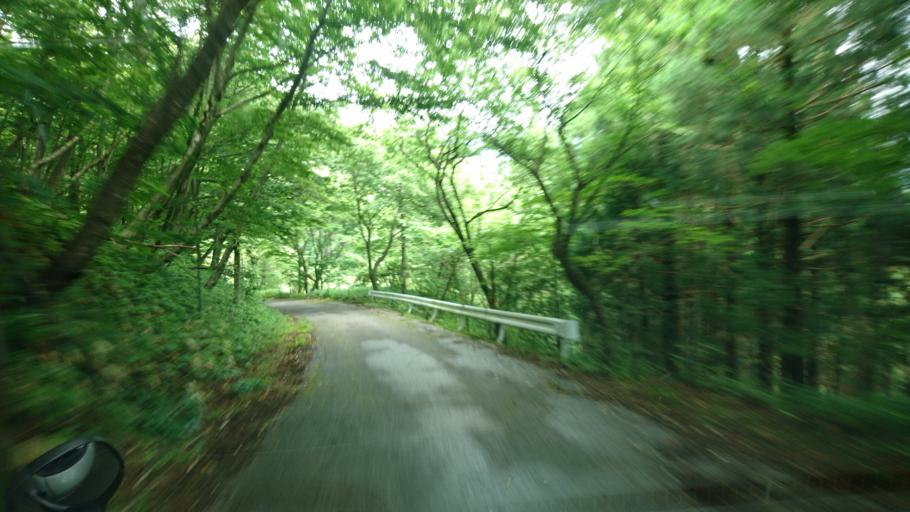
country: JP
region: Iwate
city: Ofunato
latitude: 39.1337
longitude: 141.7588
